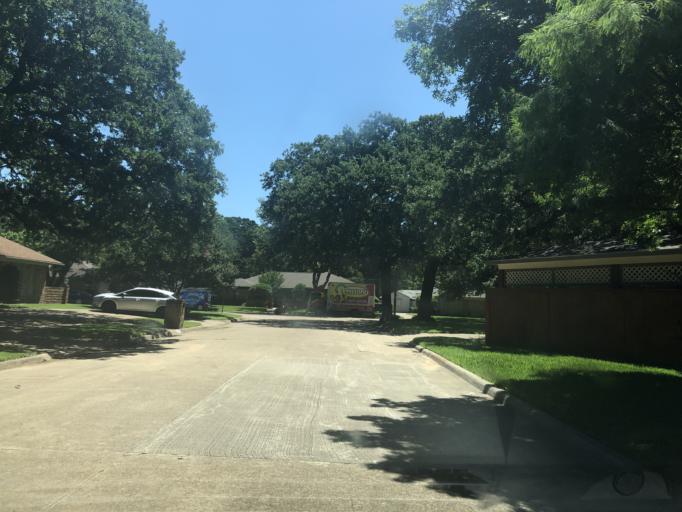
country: US
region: Texas
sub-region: Dallas County
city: Grand Prairie
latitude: 32.7743
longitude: -97.0414
